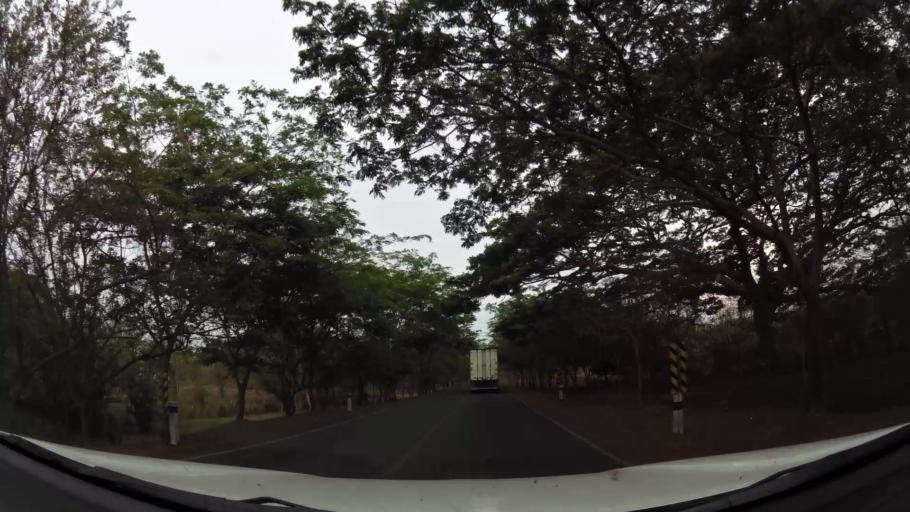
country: NI
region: Rivas
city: Cardenas
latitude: 11.2743
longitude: -85.6552
